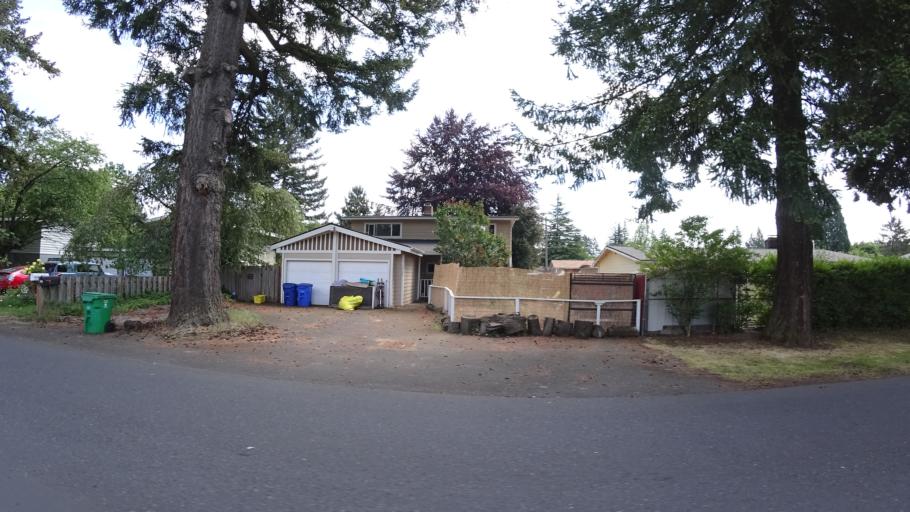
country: US
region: Oregon
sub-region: Clackamas County
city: Happy Valley
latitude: 45.4983
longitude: -122.4950
